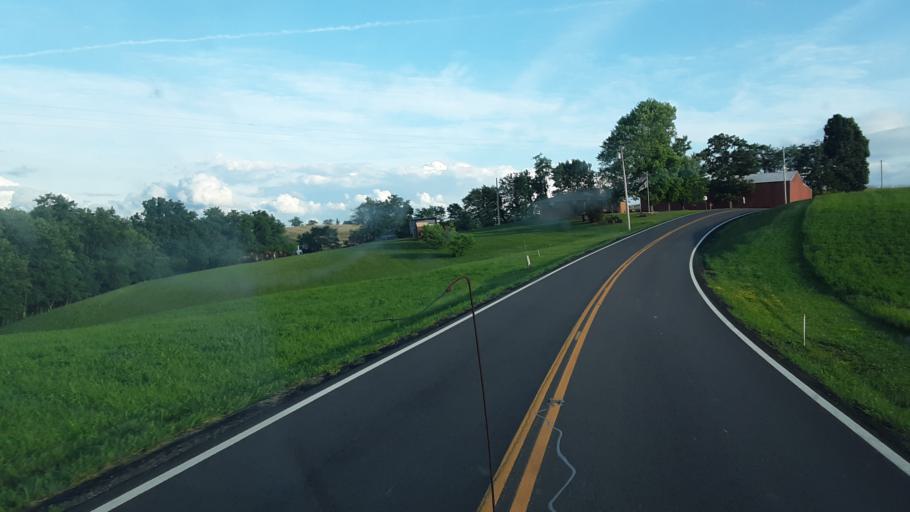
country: US
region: Ohio
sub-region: Harrison County
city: Cadiz
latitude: 40.4016
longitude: -80.9901
